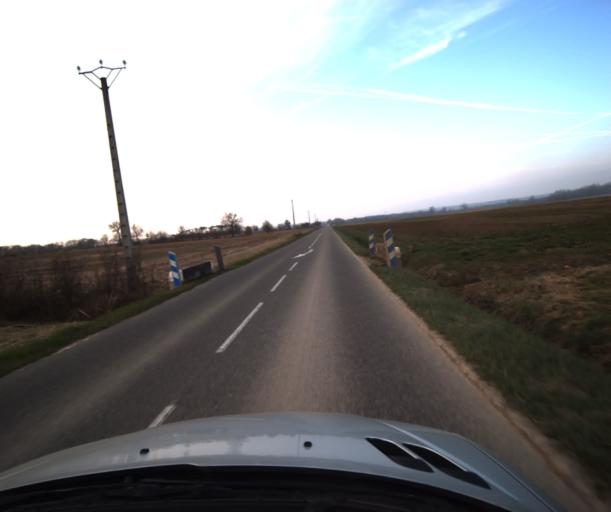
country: FR
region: Midi-Pyrenees
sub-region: Departement du Tarn-et-Garonne
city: Labastide-Saint-Pierre
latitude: 43.8916
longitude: 1.3734
